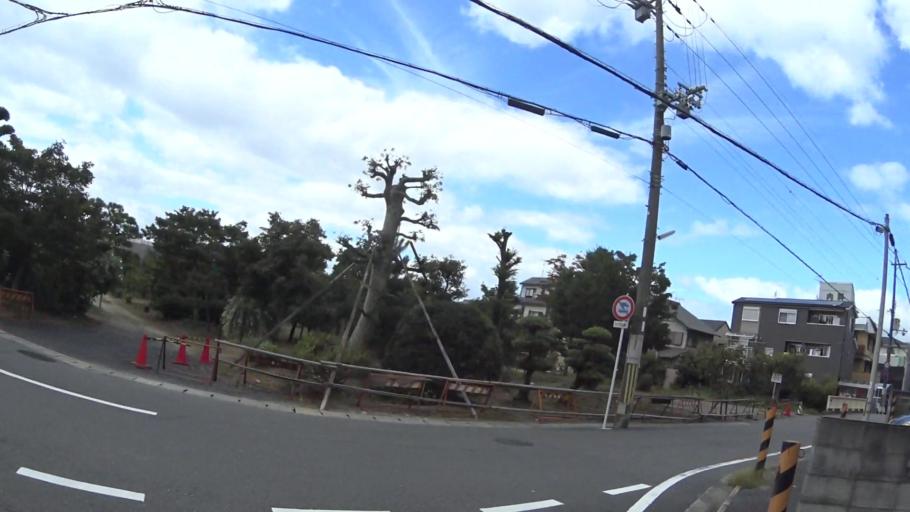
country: JP
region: Shiga Prefecture
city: Otsu-shi
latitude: 34.9821
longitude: 135.8247
